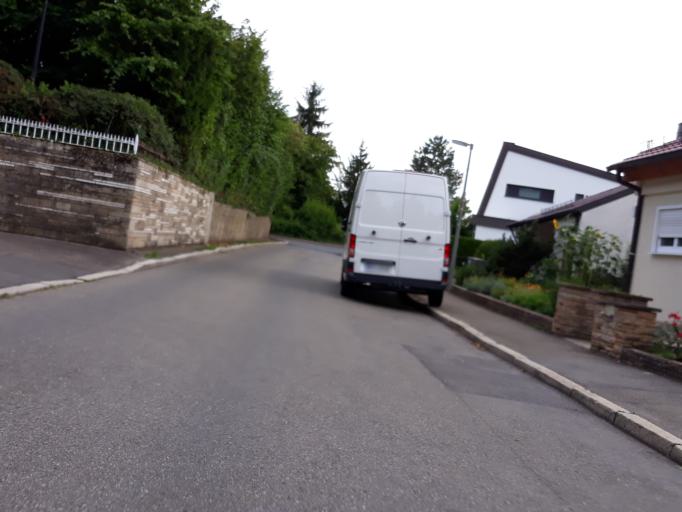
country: DE
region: Baden-Wuerttemberg
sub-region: Regierungsbezirk Stuttgart
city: Sindelfingen
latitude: 48.6878
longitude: 9.0295
